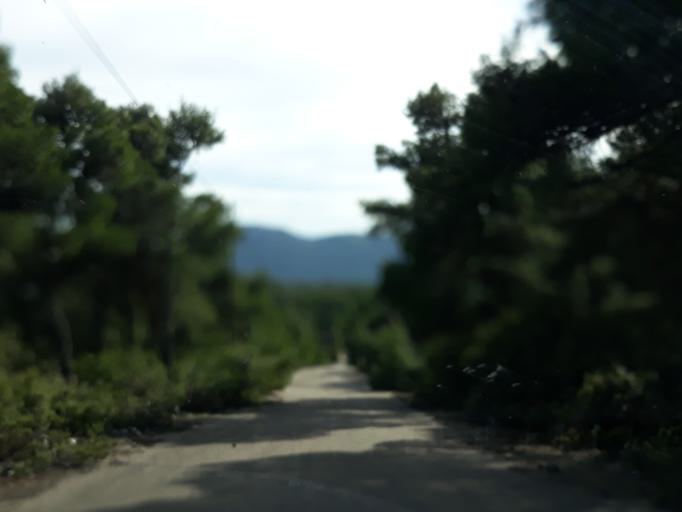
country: GR
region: Attica
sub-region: Nomarchia Anatolikis Attikis
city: Afidnes
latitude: 38.2165
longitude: 23.7950
